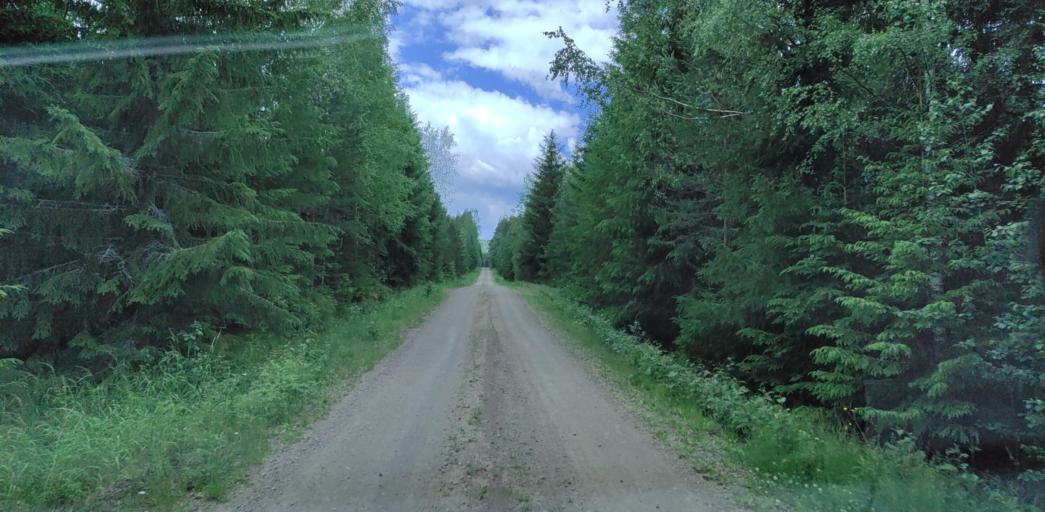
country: SE
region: Vaermland
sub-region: Hagfors Kommun
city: Ekshaerad
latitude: 60.0889
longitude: 13.4241
